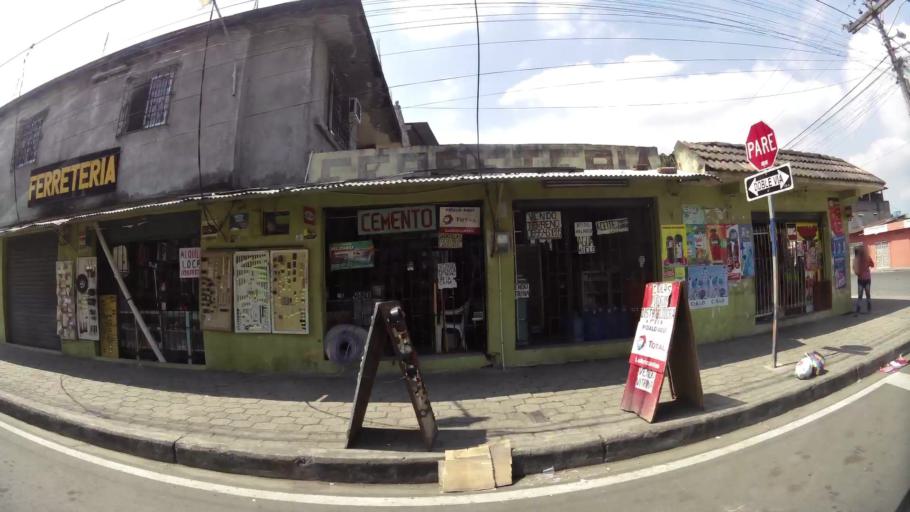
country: EC
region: Guayas
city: Eloy Alfaro
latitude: -2.1606
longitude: -79.8427
